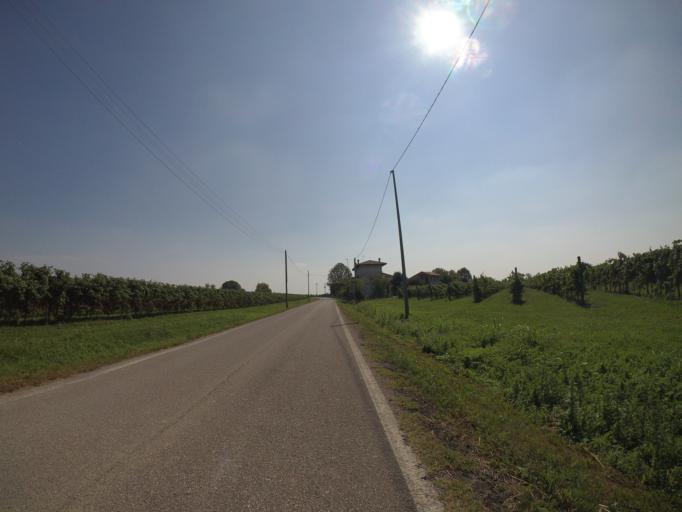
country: IT
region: Friuli Venezia Giulia
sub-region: Provincia di Udine
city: Camino al Tagliamento
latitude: 45.9191
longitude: 12.9431
